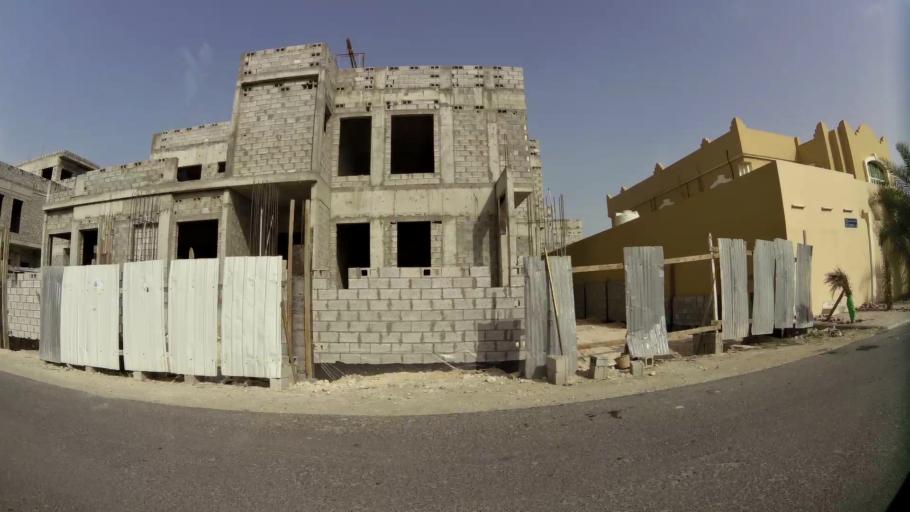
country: QA
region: Baladiyat ad Dawhah
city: Doha
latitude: 25.3236
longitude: 51.5023
